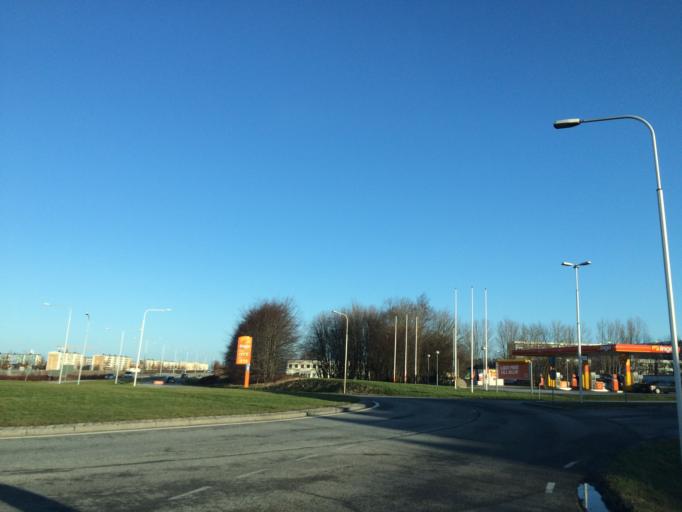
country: SE
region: Skane
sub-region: Malmo
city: Malmoe
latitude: 55.5632
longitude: 12.9849
